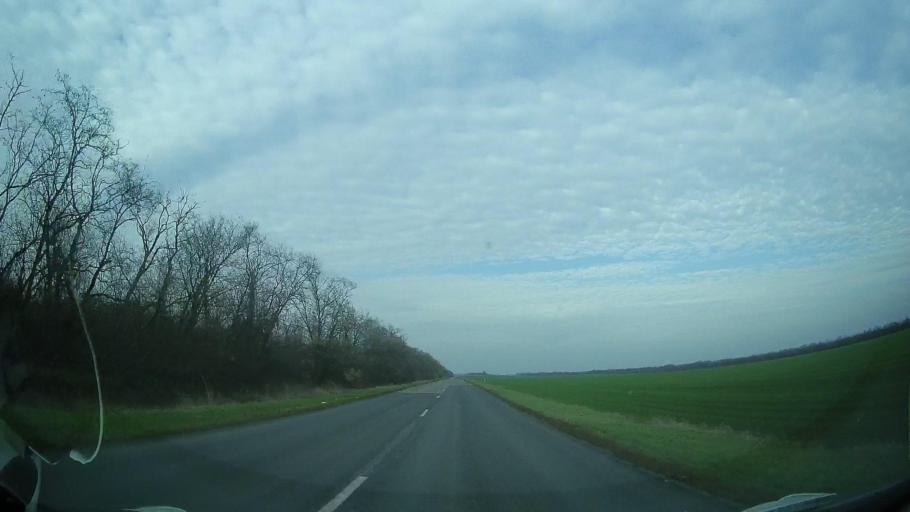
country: RU
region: Rostov
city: Zernograd
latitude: 46.9503
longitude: 40.3667
